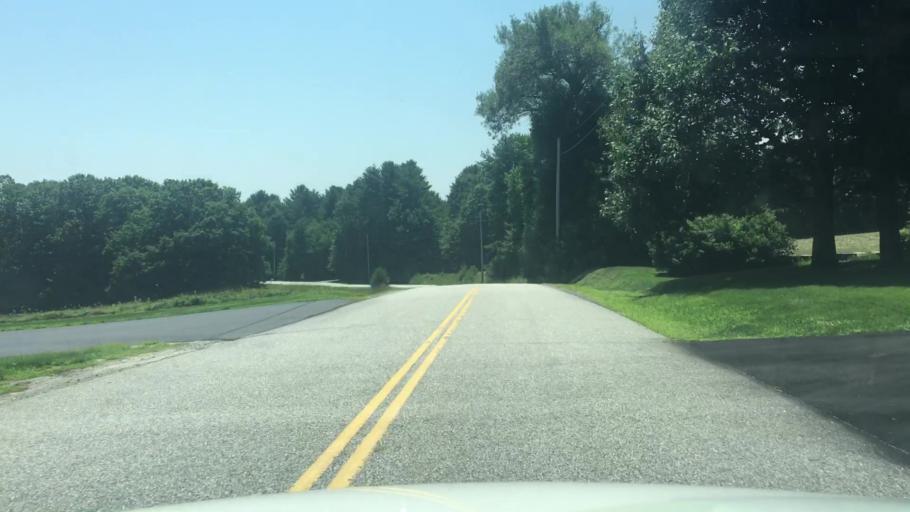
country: US
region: Maine
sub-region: Cumberland County
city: Falmouth
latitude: 43.7541
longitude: -70.2747
